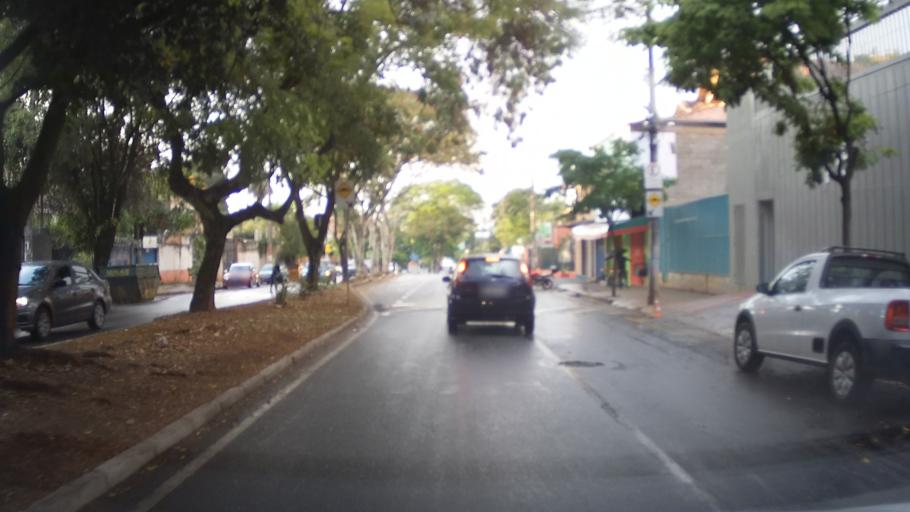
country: BR
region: Minas Gerais
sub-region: Belo Horizonte
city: Belo Horizonte
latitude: -19.9619
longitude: -43.9821
